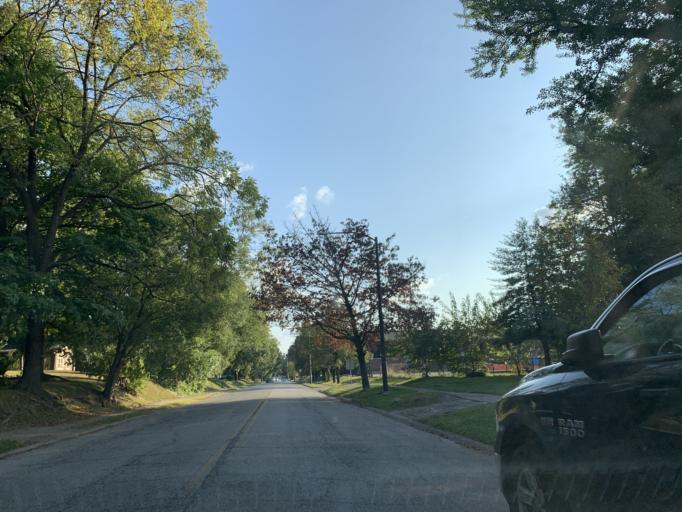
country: US
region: Kentucky
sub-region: Jefferson County
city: Audubon Park
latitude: 38.1849
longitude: -85.7640
